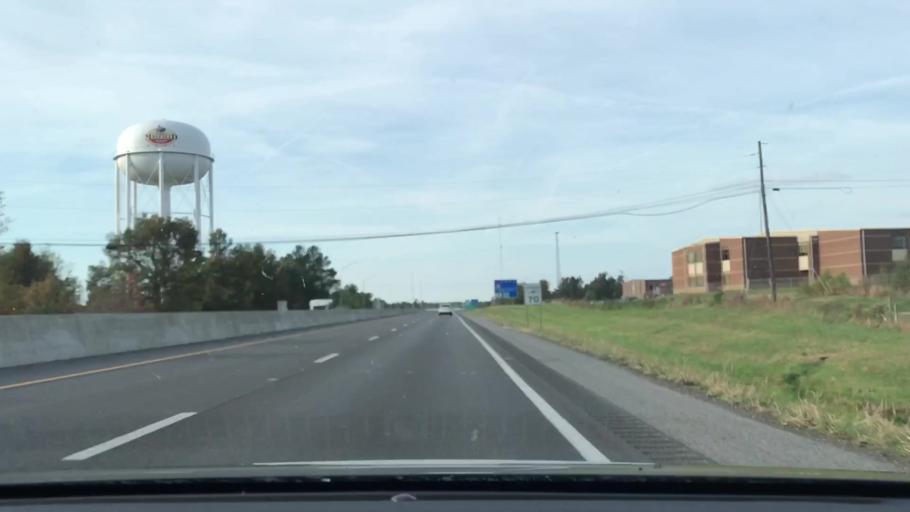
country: US
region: Kentucky
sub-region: Graves County
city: Mayfield
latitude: 36.7629
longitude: -88.6489
